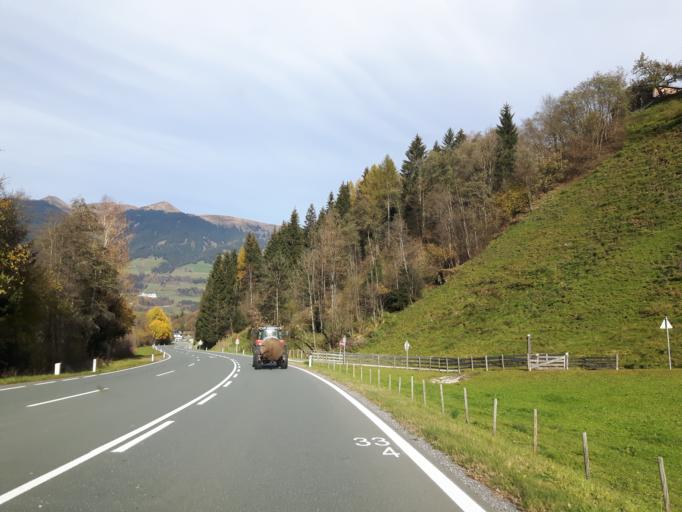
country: AT
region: Salzburg
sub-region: Politischer Bezirk Zell am See
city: Mittersill
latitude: 47.2609
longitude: 12.4845
